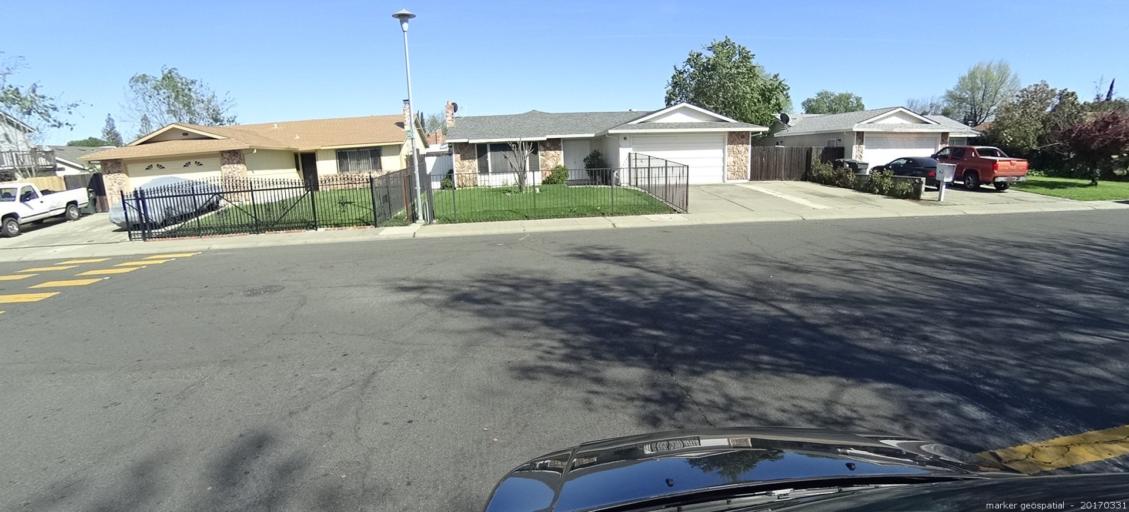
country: US
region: California
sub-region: Sacramento County
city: Laguna
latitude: 38.4540
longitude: -121.4361
